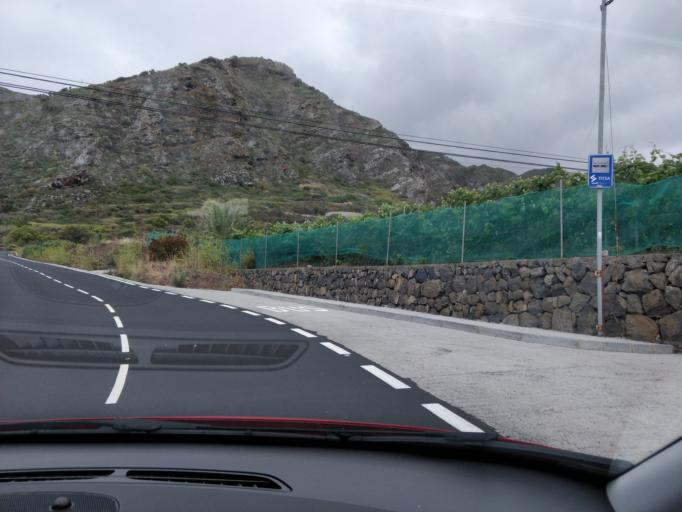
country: ES
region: Canary Islands
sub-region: Provincia de Santa Cruz de Tenerife
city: Tanque
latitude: 28.3545
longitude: -16.8455
